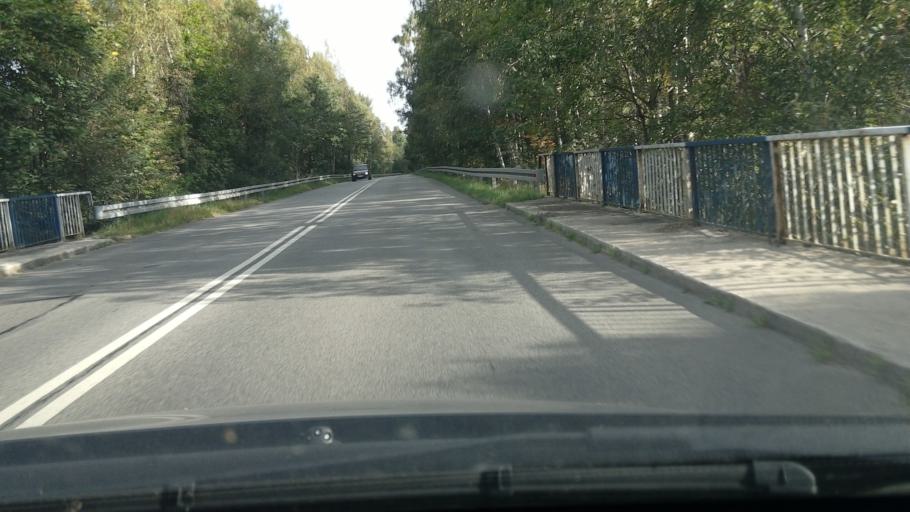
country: PL
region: Lower Silesian Voivodeship
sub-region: Powiat jeleniogorski
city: Myslakowice
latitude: 50.8183
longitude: 15.7732
